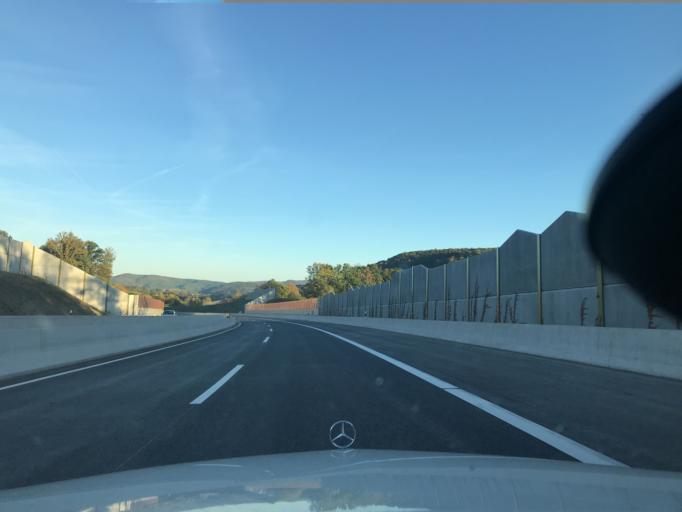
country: DE
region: Hesse
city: Waldkappel
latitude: 51.1532
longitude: 9.8944
